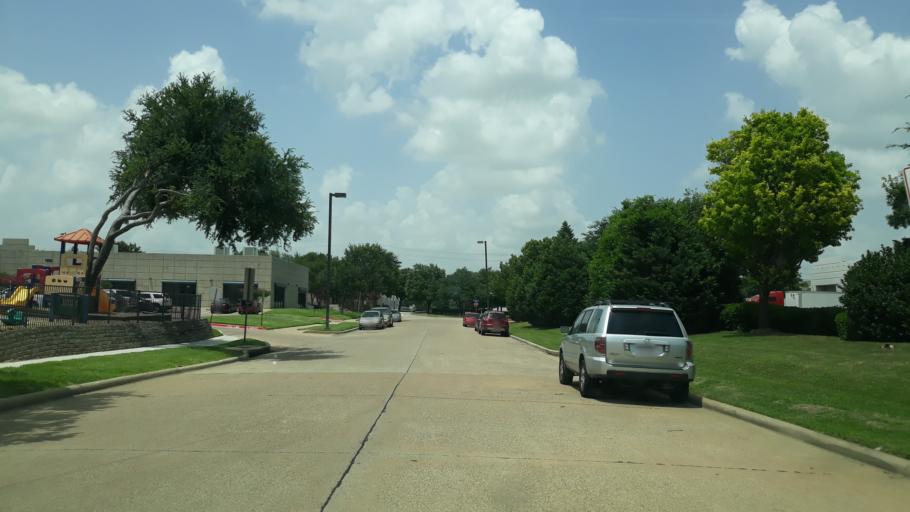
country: US
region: Texas
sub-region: Dallas County
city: Coppell
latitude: 32.9386
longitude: -97.0004
